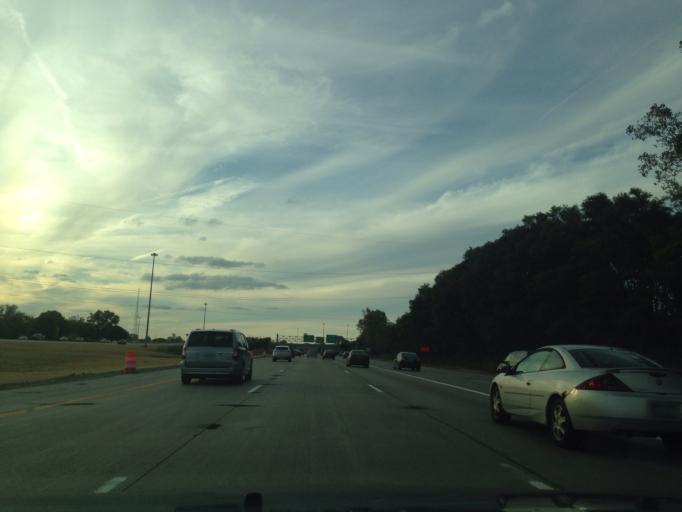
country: US
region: Michigan
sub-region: Wayne County
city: Plymouth
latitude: 42.3836
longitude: -83.4254
